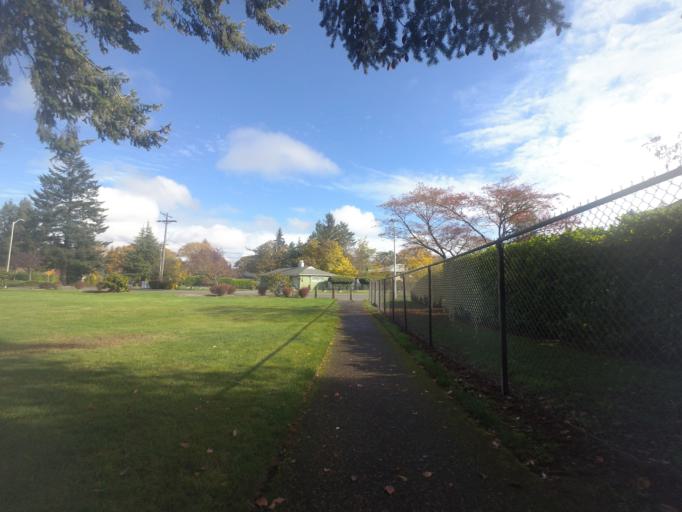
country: US
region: Washington
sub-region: Pierce County
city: Lakewood
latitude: 47.1750
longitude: -122.5162
